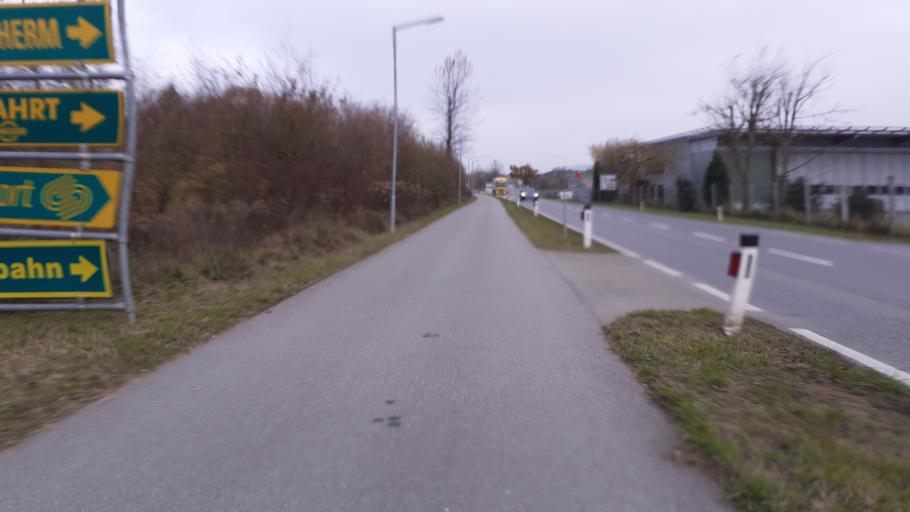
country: AT
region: Vorarlberg
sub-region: Politischer Bezirk Feldkirch
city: Nofels
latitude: 47.2742
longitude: 9.5906
